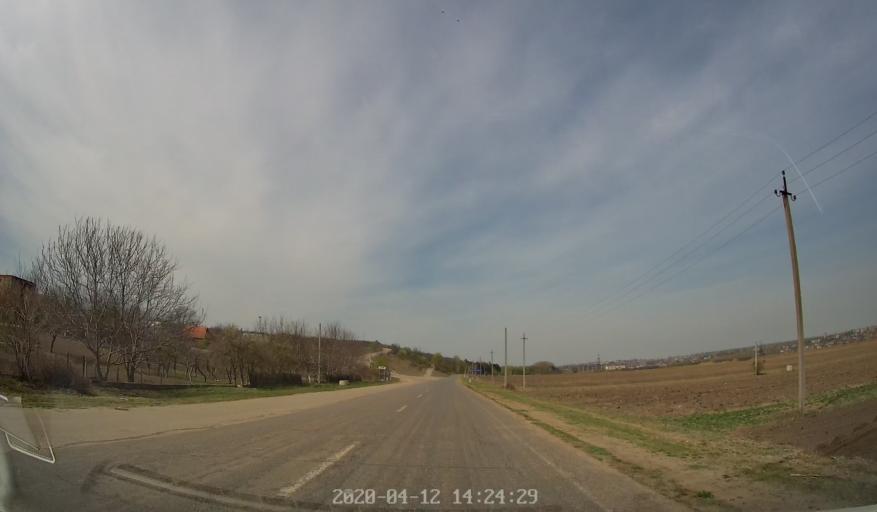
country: MD
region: Telenesti
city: Dubasari
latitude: 47.2626
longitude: 29.1288
